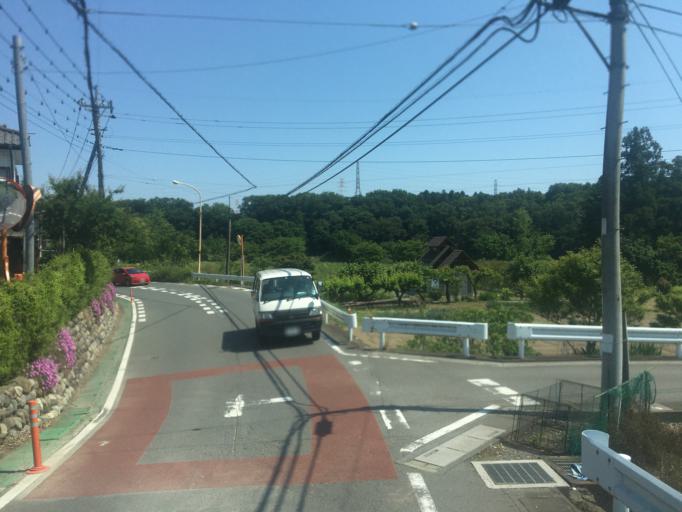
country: JP
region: Saitama
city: Ogawa
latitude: 36.0306
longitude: 139.3317
